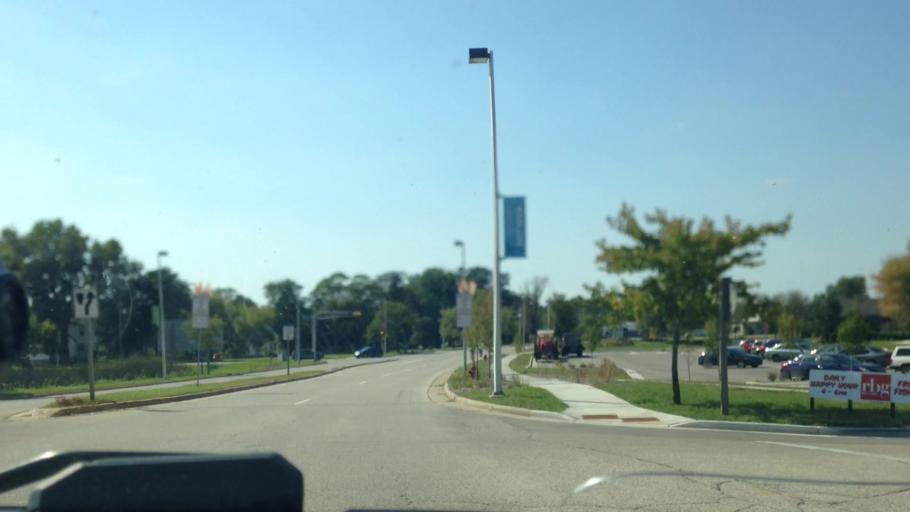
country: US
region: Wisconsin
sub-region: Waukesha County
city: Menomonee Falls
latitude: 43.1773
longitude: -88.0931
